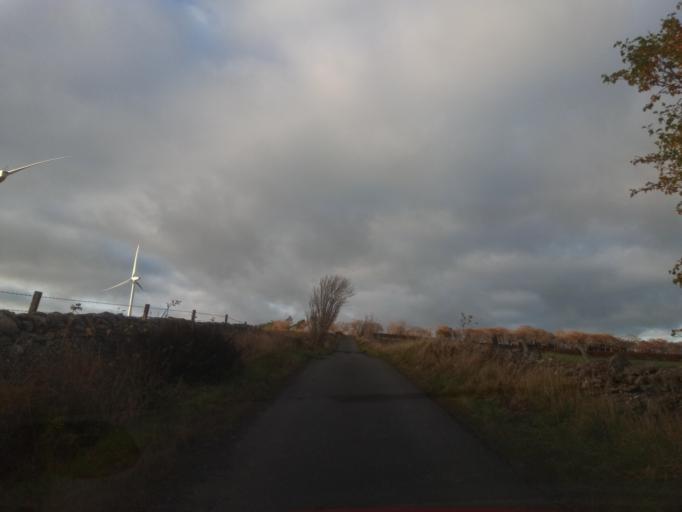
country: GB
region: Scotland
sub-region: The Scottish Borders
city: Galashiels
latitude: 55.6696
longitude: -2.8169
